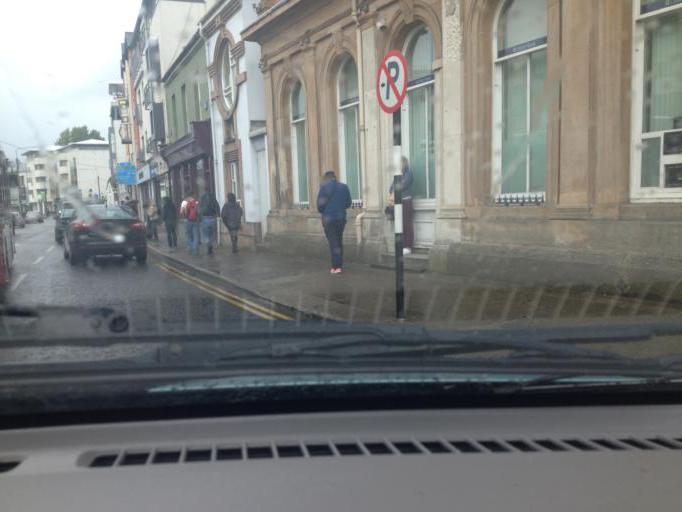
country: IE
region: Connaught
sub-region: Sligo
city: Sligo
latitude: 54.2726
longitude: -8.4740
